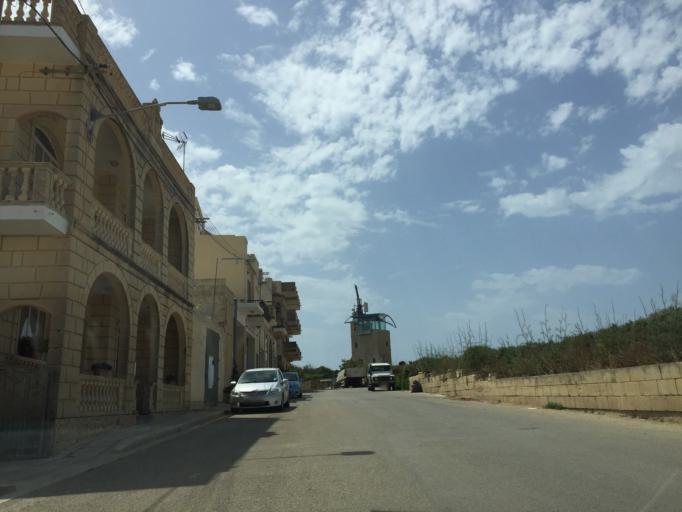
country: MT
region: In-Nadur
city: Nadur
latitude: 36.0368
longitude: 14.2838
